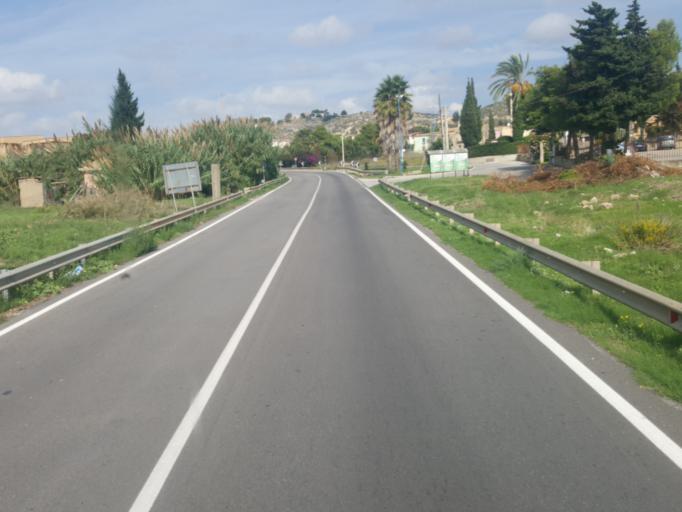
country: IT
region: Sicily
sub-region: Agrigento
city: Porto Empedocle
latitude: 37.2957
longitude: 13.4972
